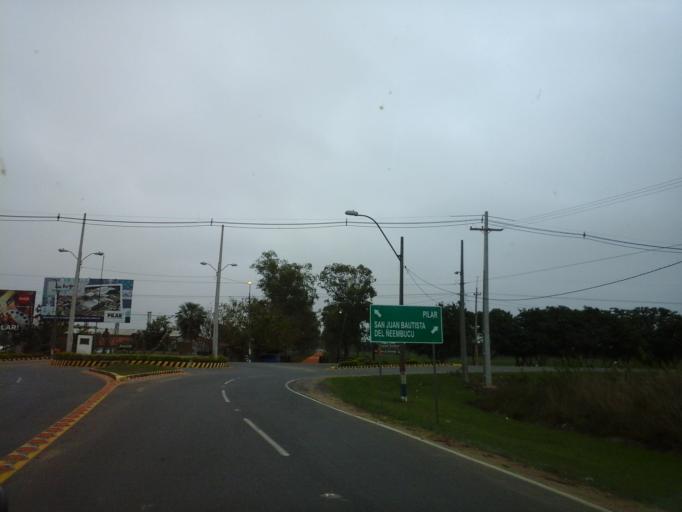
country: PY
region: Neembucu
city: Pilar
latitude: -26.8396
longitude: -58.2895
